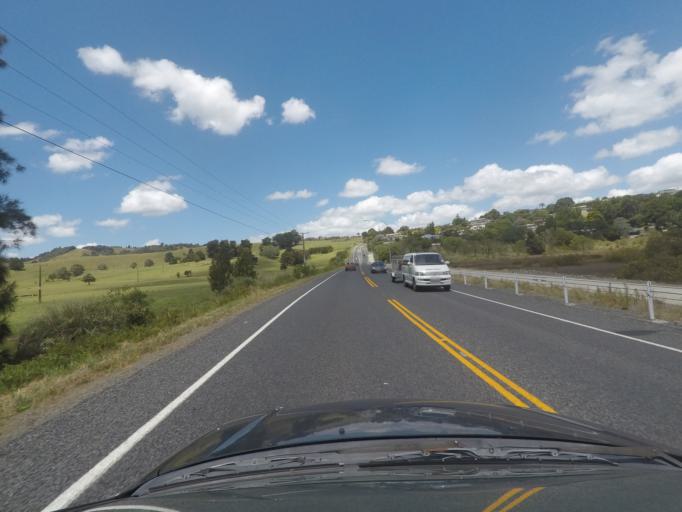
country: NZ
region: Northland
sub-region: Whangarei
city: Whangarei
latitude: -35.7396
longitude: 174.3616
